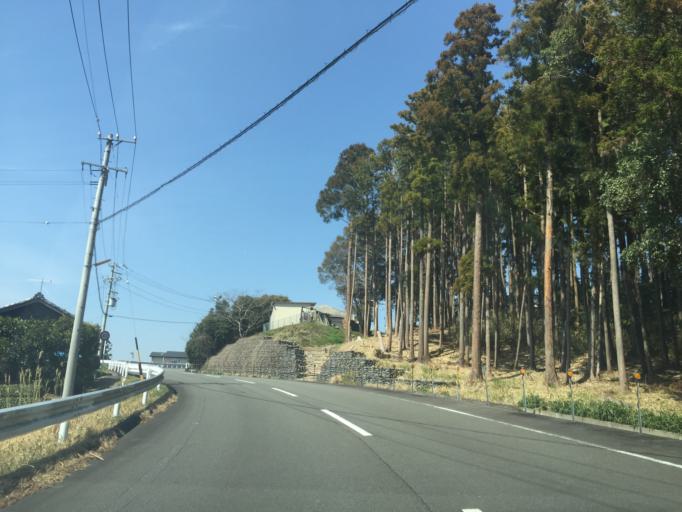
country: JP
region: Shizuoka
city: Kanaya
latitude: 34.8026
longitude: 138.1249
